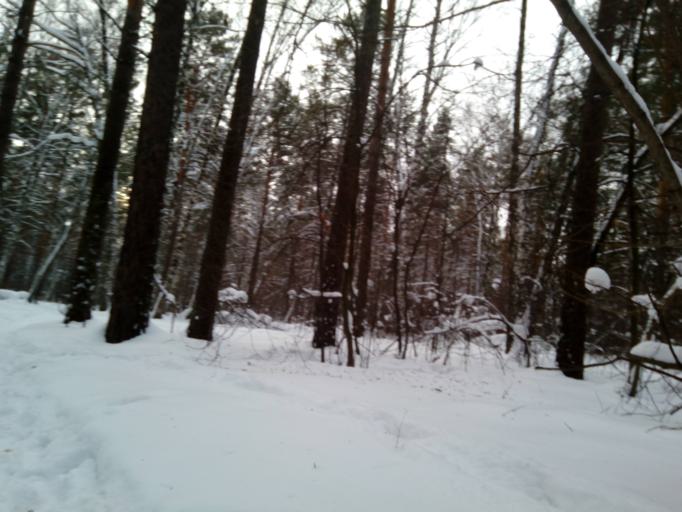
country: RU
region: Novosibirsk
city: Akademgorodok
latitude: 54.8586
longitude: 83.0929
